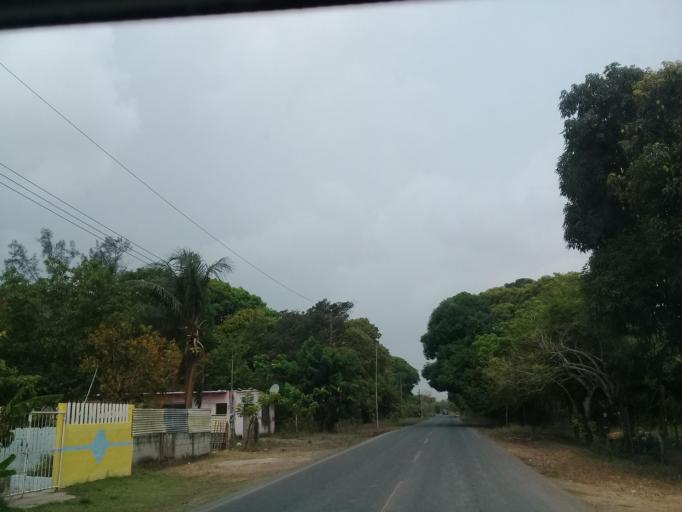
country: MX
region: Veracruz
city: El Tejar
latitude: 19.0547
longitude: -96.1936
